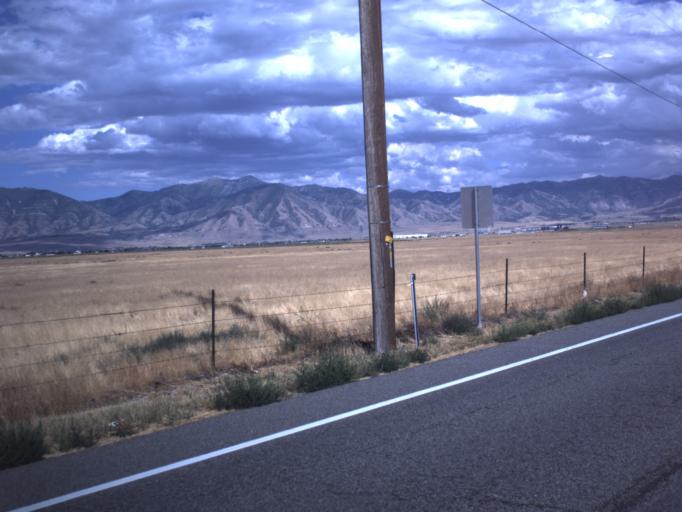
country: US
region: Utah
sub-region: Tooele County
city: Grantsville
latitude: 40.5881
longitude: -112.4152
